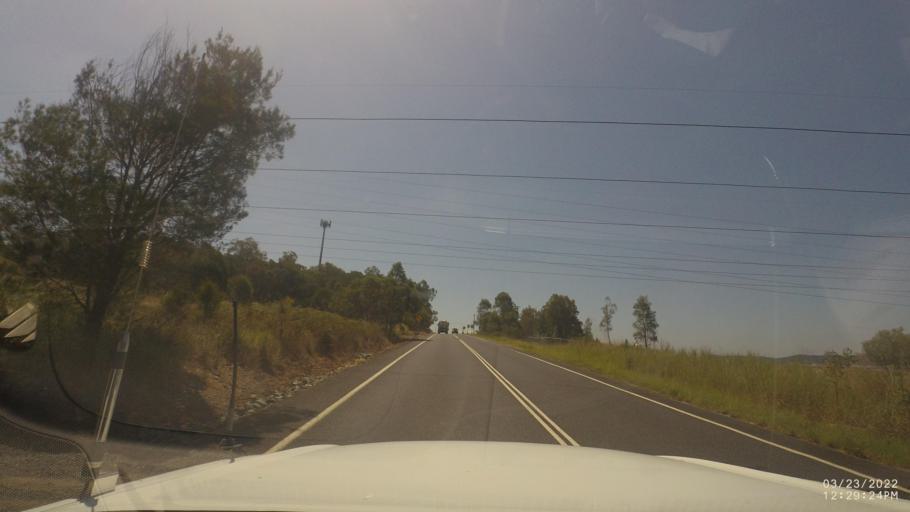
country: AU
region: Queensland
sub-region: Logan
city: Chambers Flat
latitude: -27.8050
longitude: 153.0979
